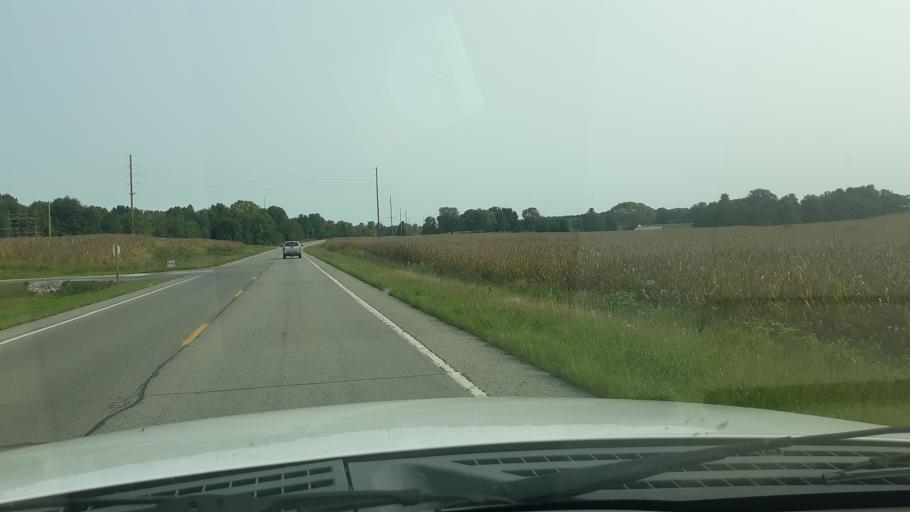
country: US
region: Illinois
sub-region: White County
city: Norris City
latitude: 37.9749
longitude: -88.3194
